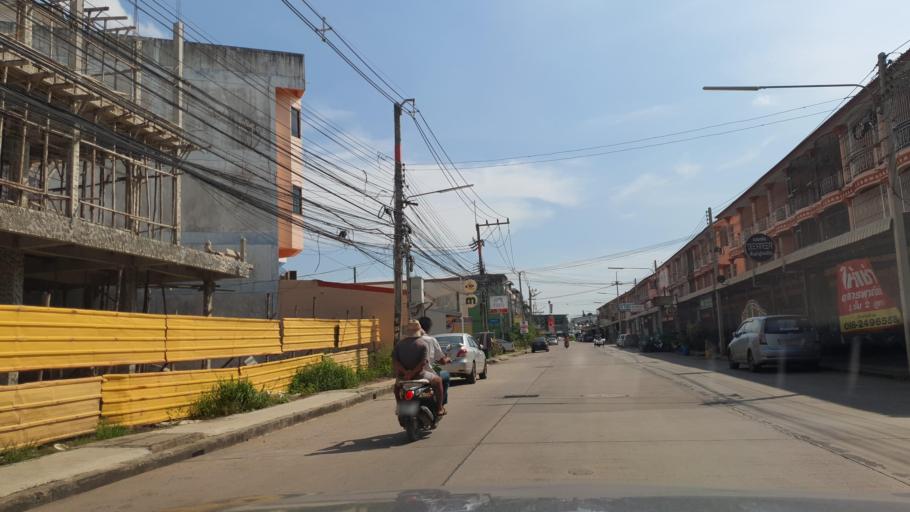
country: TH
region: Chachoengsao
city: Chachoengsao
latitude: 13.6797
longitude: 101.0628
